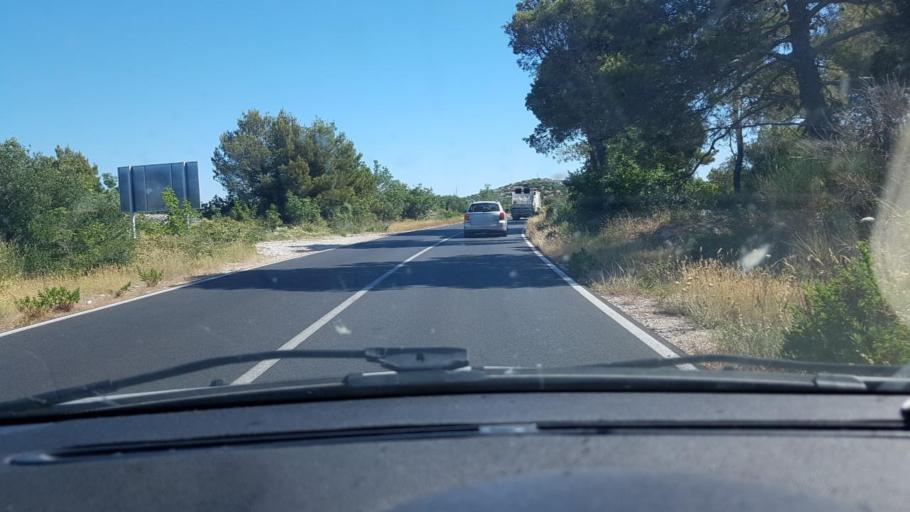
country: HR
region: Sibensko-Kniniska
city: Zaton
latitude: 43.7595
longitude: 15.8163
